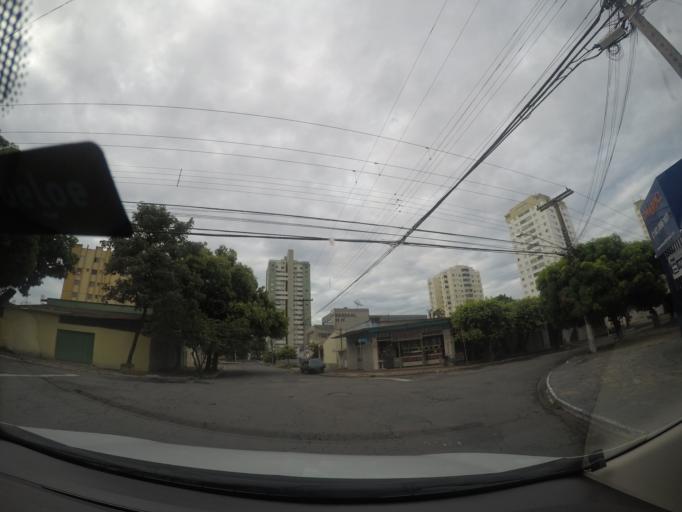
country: BR
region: Goias
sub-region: Goiania
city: Goiania
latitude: -16.6682
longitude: -49.2660
